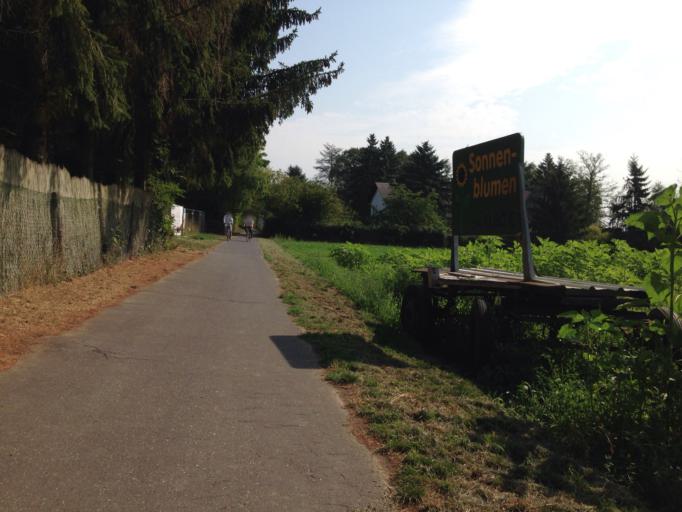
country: DE
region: Hesse
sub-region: Regierungsbezirk Giessen
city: Giessen
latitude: 50.6003
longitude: 8.7037
